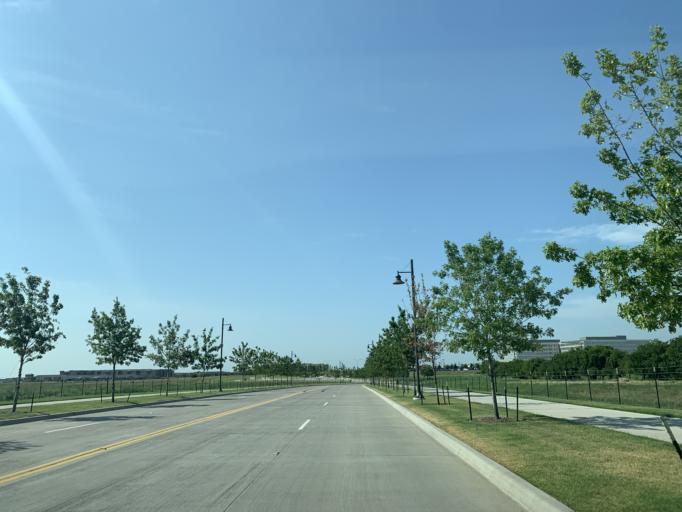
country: US
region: Texas
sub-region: Tarrant County
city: Haslet
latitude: 32.9265
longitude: -97.3127
